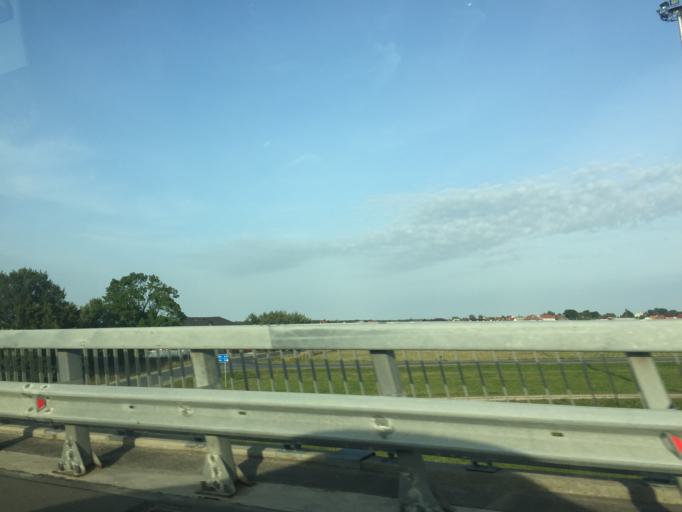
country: RU
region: Kaliningrad
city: Gur'yevsk
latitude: 54.8562
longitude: 20.5674
